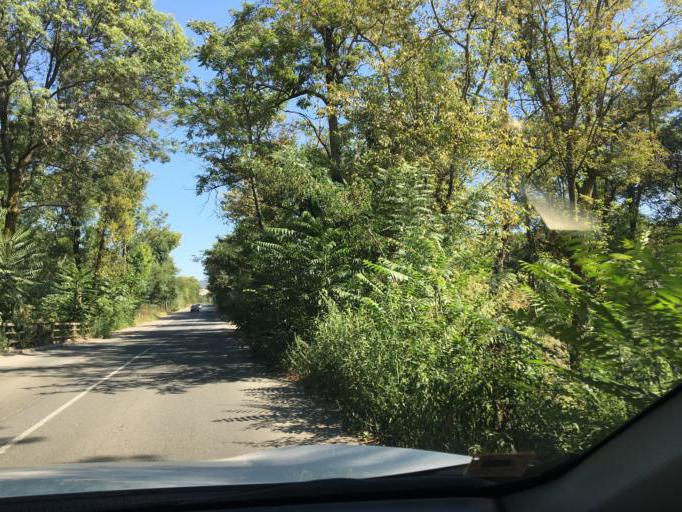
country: BG
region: Burgas
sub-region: Obshtina Kameno
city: Kameno
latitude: 42.6116
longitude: 27.3926
